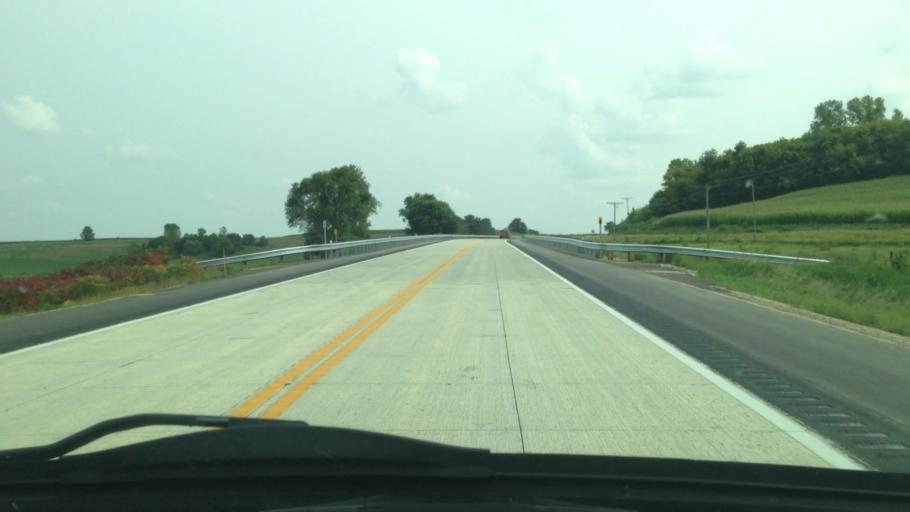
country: US
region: Minnesota
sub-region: Olmsted County
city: Oronoco
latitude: 44.1463
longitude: -92.4173
